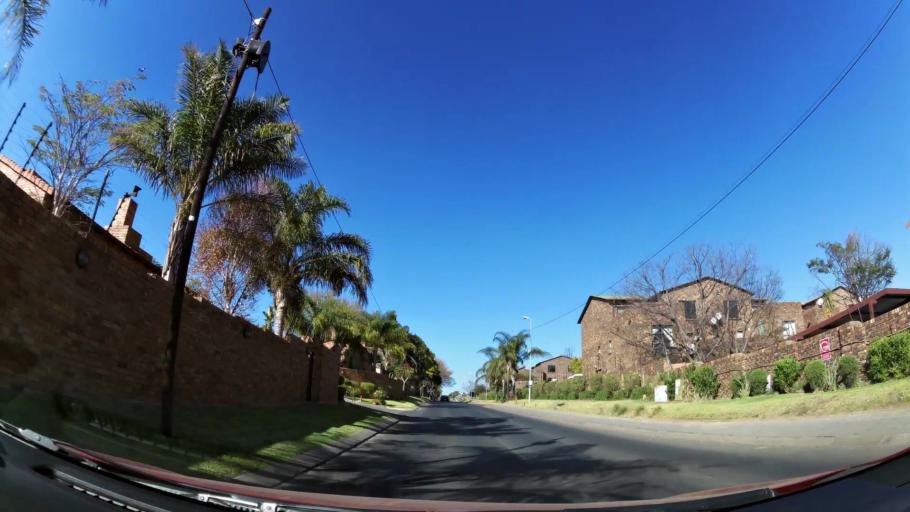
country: ZA
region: Gauteng
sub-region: City of Johannesburg Metropolitan Municipality
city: Diepsloot
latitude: -26.0425
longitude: 27.9698
